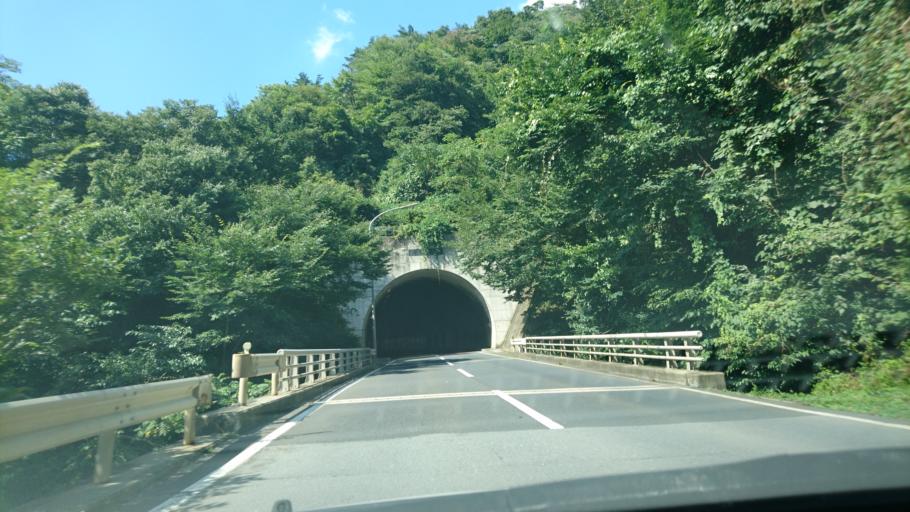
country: JP
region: Iwate
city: Ofunato
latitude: 39.0147
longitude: 141.4732
